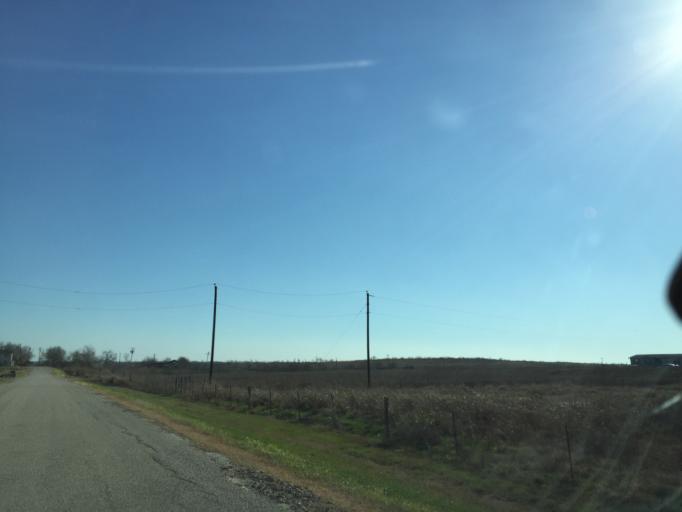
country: US
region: Texas
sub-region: Williamson County
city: Taylor
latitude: 30.5612
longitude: -97.3060
